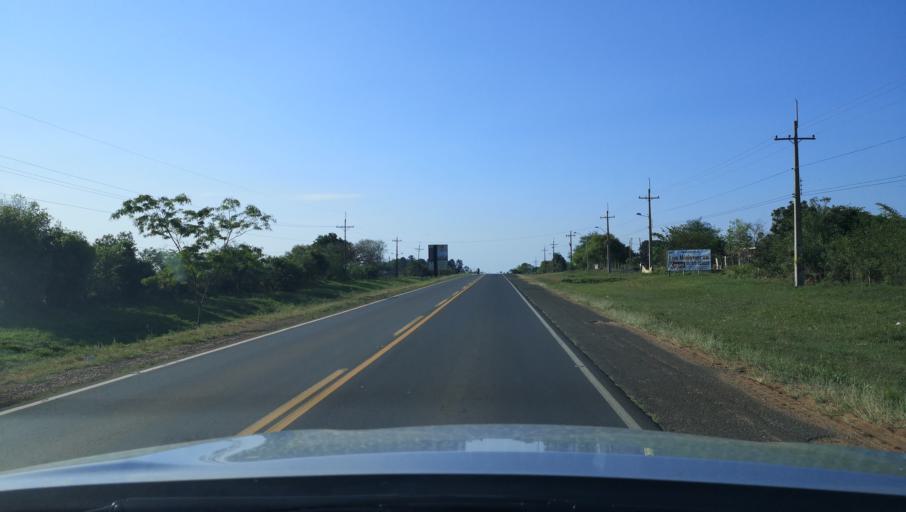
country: PY
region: Misiones
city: Santa Maria
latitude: -26.8549
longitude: -57.0356
